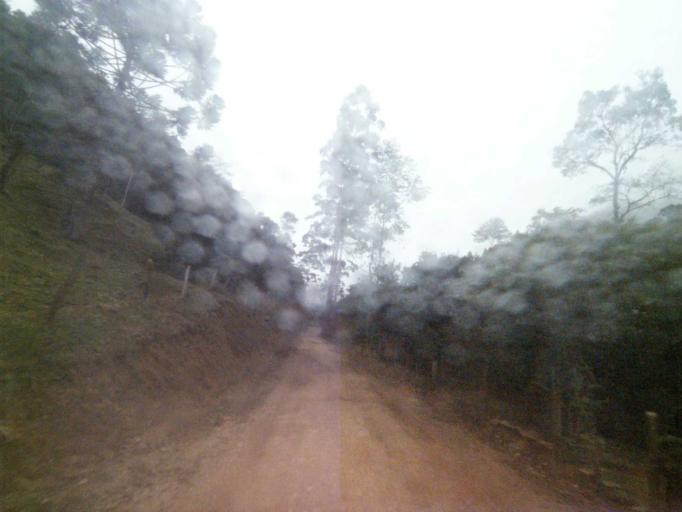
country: BR
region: Santa Catarina
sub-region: Anitapolis
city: Anitapolis
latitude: -27.8656
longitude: -49.1315
